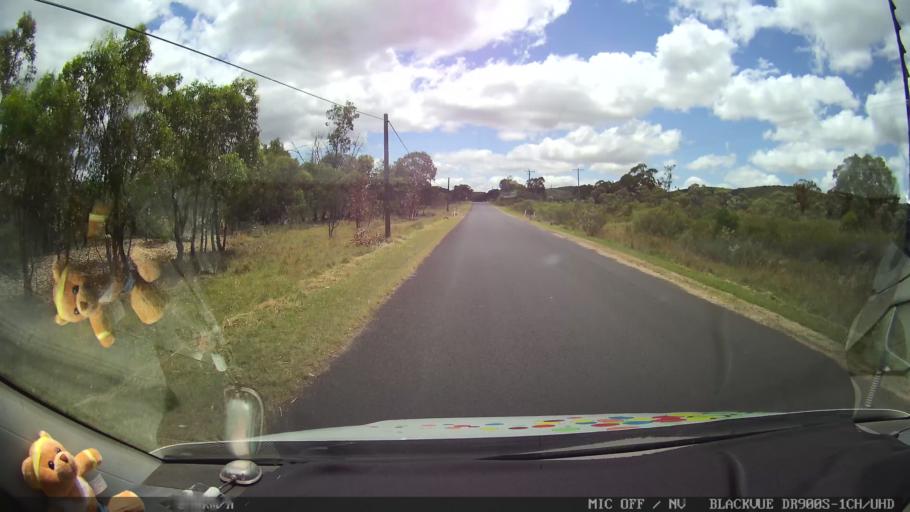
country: AU
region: New South Wales
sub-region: Glen Innes Severn
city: Glen Innes
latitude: -29.4427
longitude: 151.6073
